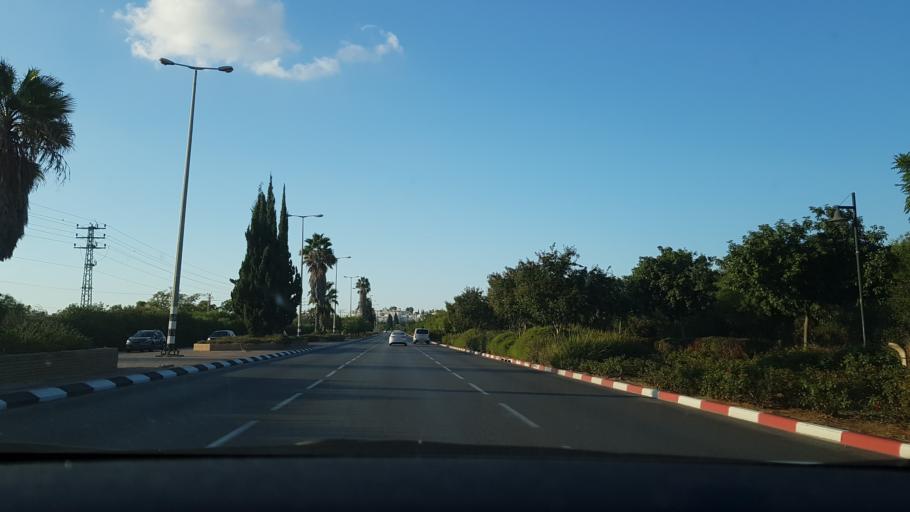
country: IL
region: Central District
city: Ness Ziona
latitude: 31.9165
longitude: 34.8004
